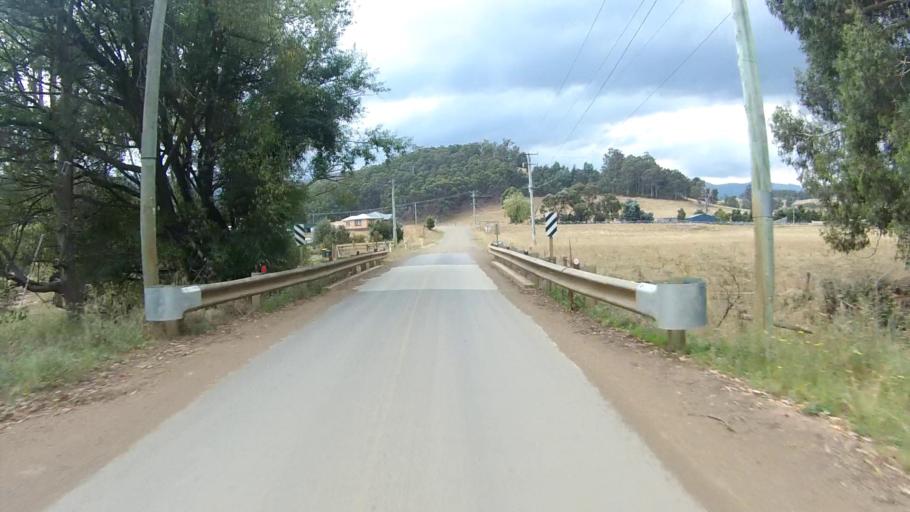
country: AU
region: Tasmania
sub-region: Huon Valley
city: Huonville
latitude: -42.9796
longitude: 147.0544
